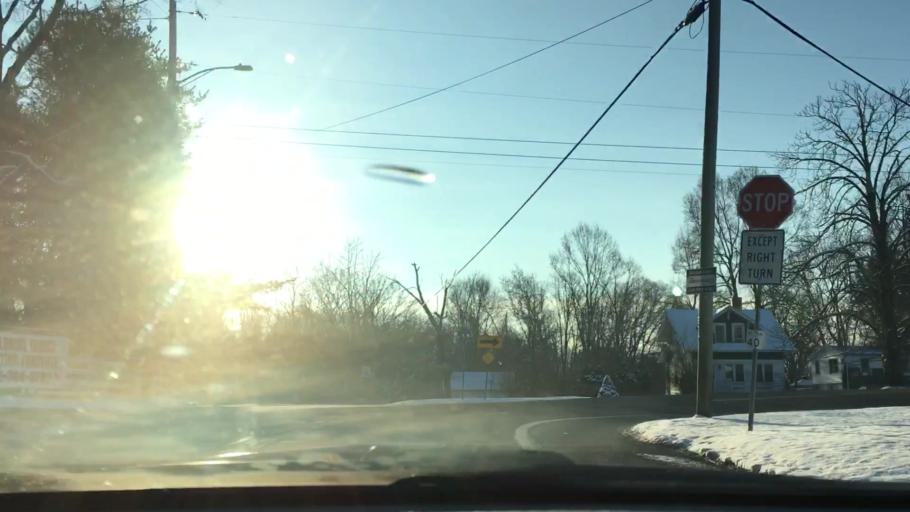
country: US
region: Pennsylvania
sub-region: Allegheny County
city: Elizabeth
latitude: 40.2559
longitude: -79.8457
